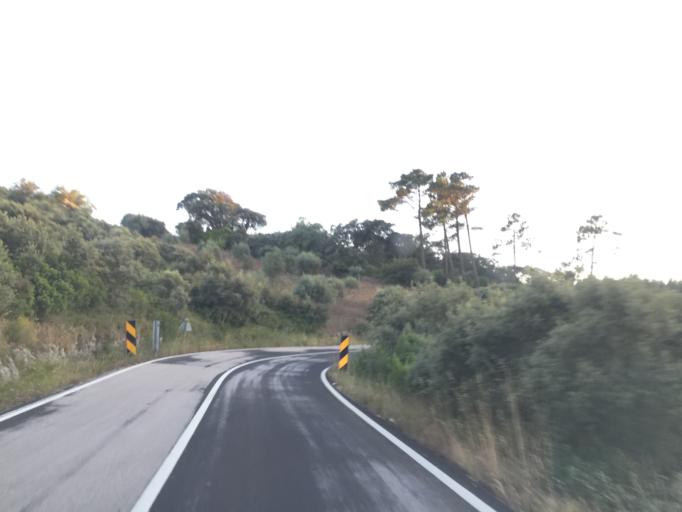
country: PT
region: Santarem
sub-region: Ourem
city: Fatima
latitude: 39.6293
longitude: -8.6269
